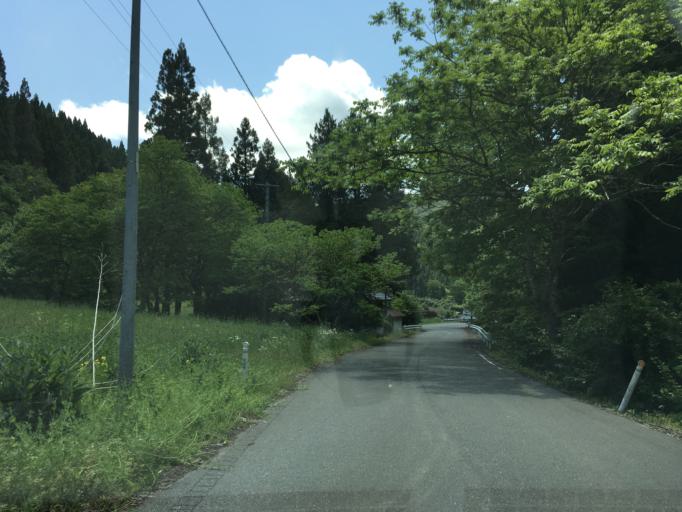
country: JP
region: Miyagi
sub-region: Oshika Gun
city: Onagawa Cho
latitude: 38.6753
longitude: 141.3634
